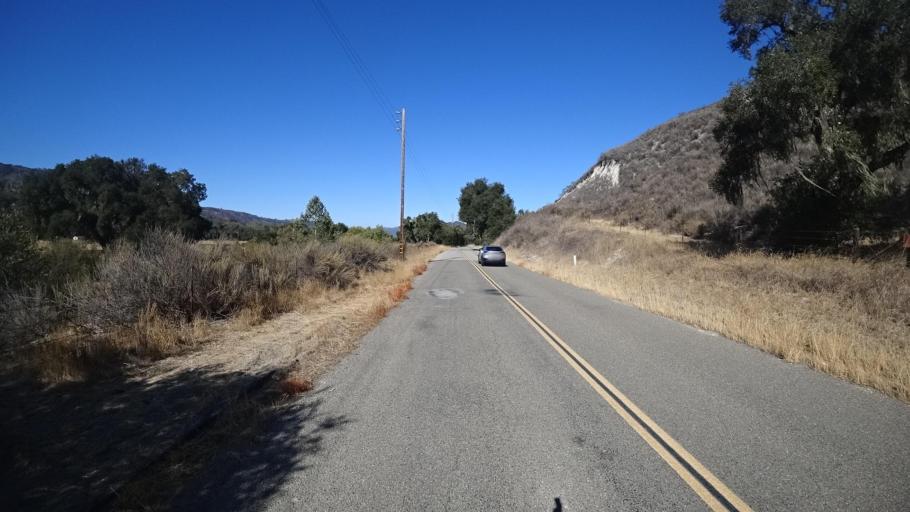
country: US
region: California
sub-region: Monterey County
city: Carmel Valley Village
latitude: 36.4378
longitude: -121.6311
